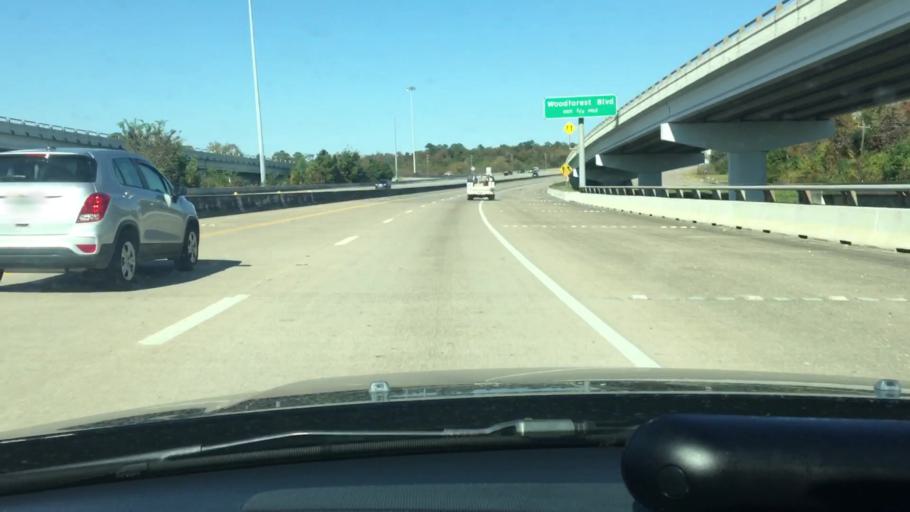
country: US
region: Texas
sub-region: Harris County
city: Cloverleaf
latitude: 29.7755
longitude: -95.1570
